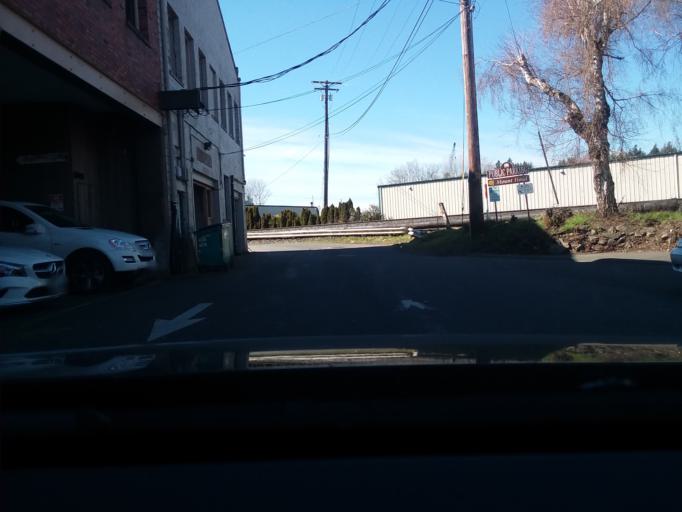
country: US
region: Washington
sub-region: Pierce County
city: Sumner
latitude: 47.2037
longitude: -122.2414
